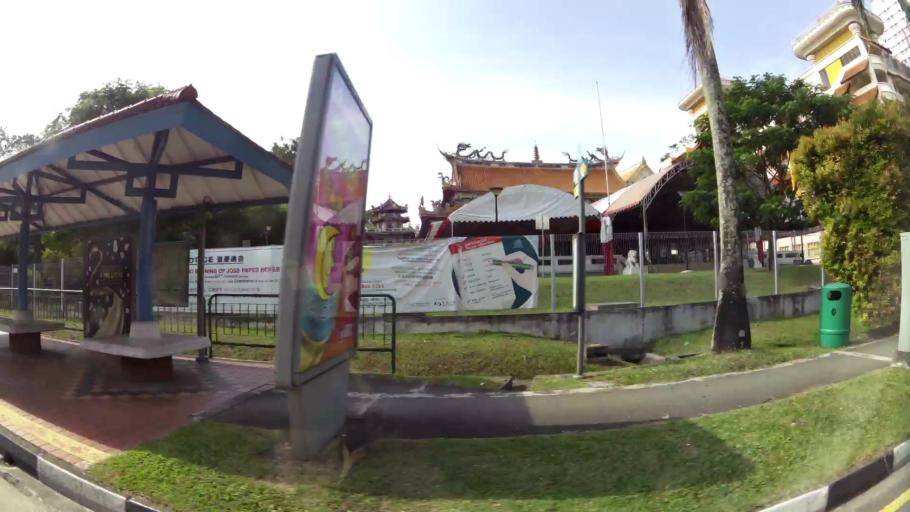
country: SG
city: Singapore
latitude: 1.3629
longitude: 103.8369
